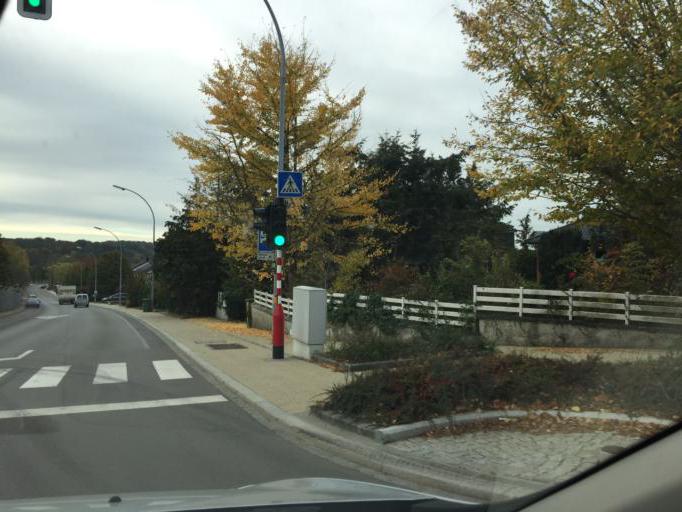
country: LU
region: Luxembourg
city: Capellen
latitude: 49.6439
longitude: 5.9841
